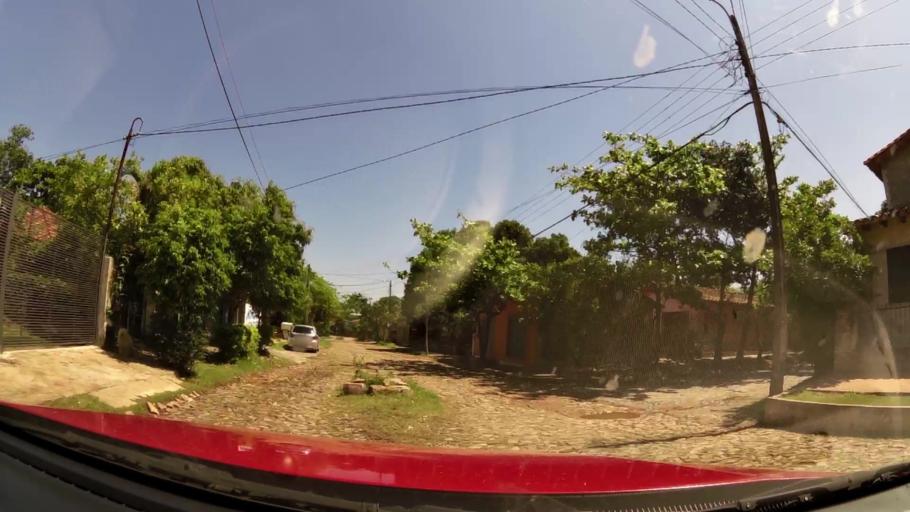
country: PY
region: Central
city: Colonia Mariano Roque Alonso
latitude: -25.2457
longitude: -57.5517
